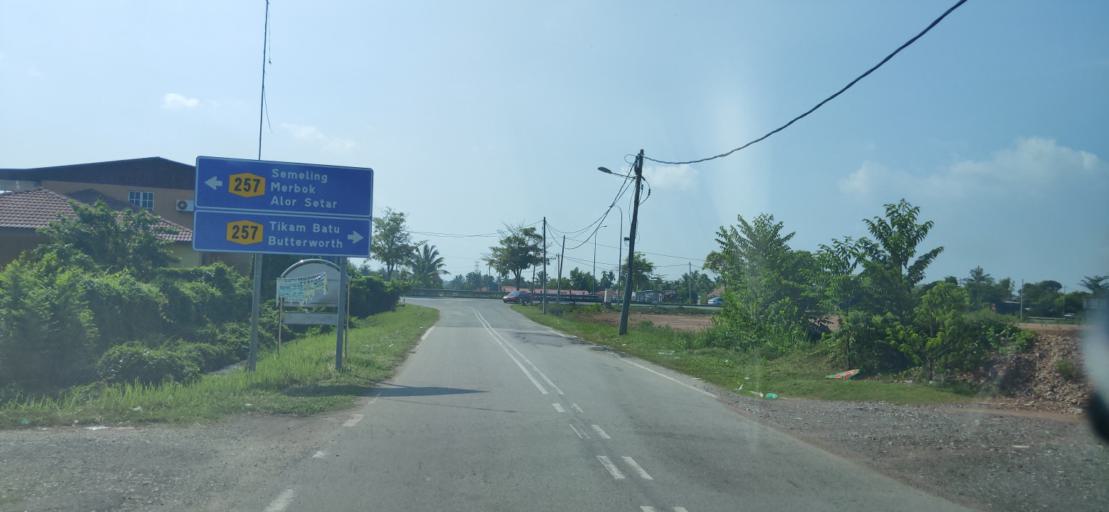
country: MY
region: Kedah
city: Sungai Petani
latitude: 5.6610
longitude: 100.4643
